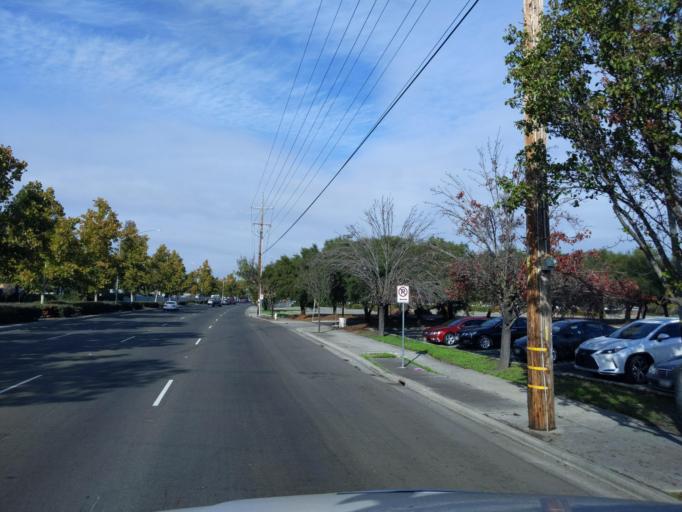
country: US
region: California
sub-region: San Joaquin County
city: Lincoln Village
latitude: 38.0121
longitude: -121.2943
